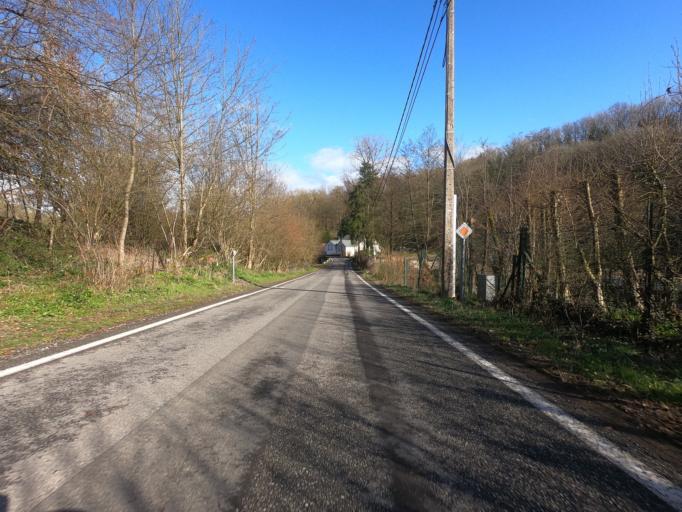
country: BE
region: Wallonia
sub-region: Province de Namur
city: Mettet
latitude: 50.3009
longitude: 4.7331
